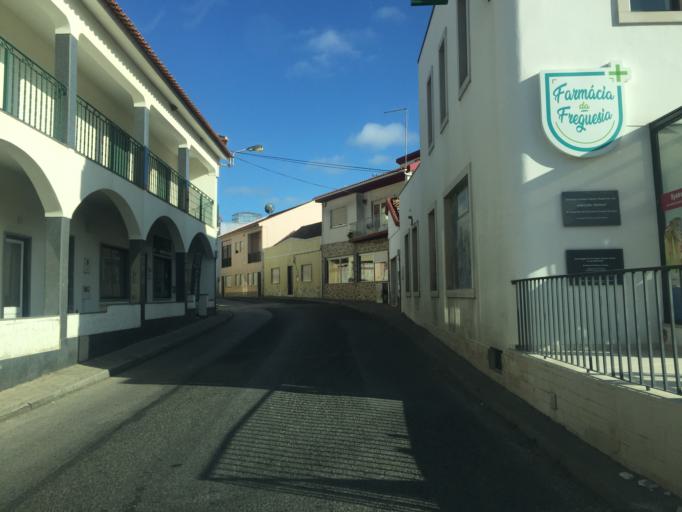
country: PT
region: Lisbon
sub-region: Torres Vedras
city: A dos Cunhados
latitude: 39.1509
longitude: -9.2980
